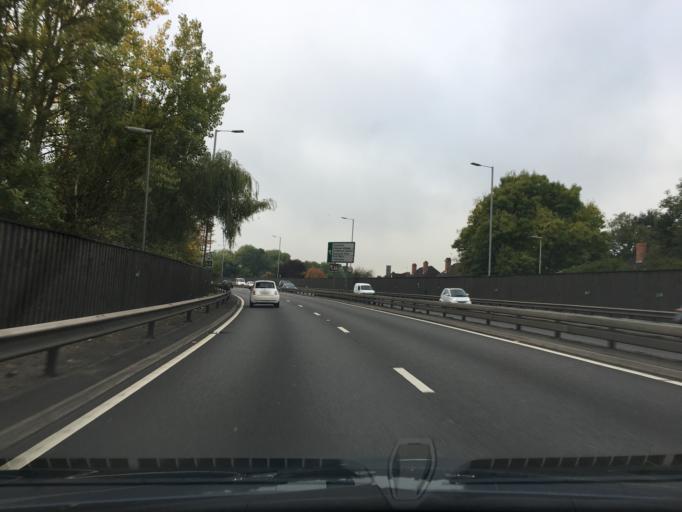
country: GB
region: England
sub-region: Surrey
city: Guildford
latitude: 51.2460
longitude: -0.5955
